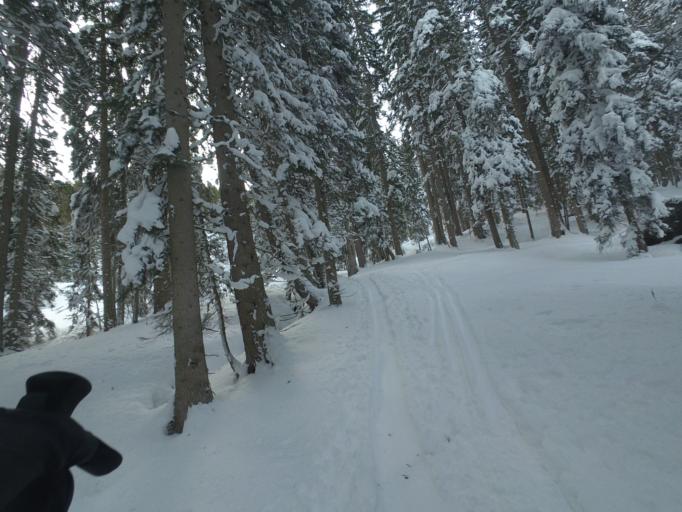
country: AT
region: Salzburg
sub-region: Politischer Bezirk Zell am See
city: Lend
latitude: 47.2727
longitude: 13.0156
